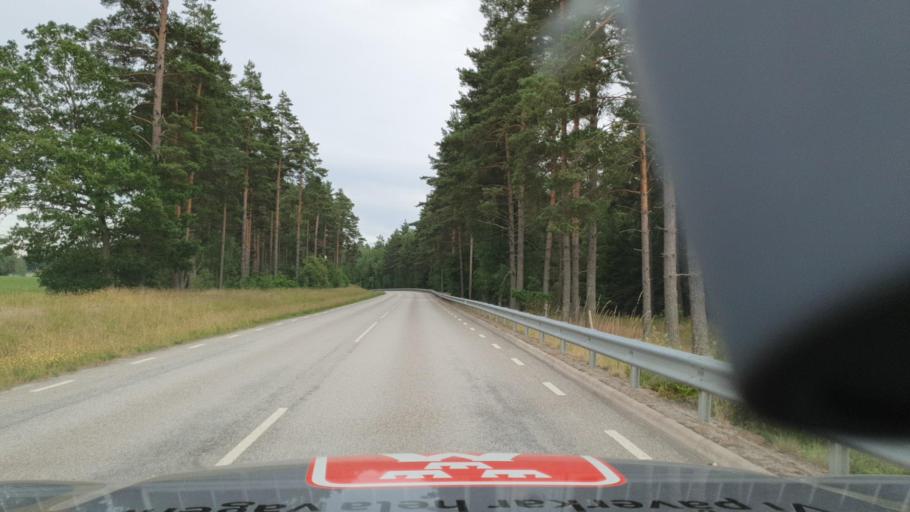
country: SE
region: Kalmar
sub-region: Nybro Kommun
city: Nybro
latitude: 56.7076
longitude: 15.9707
